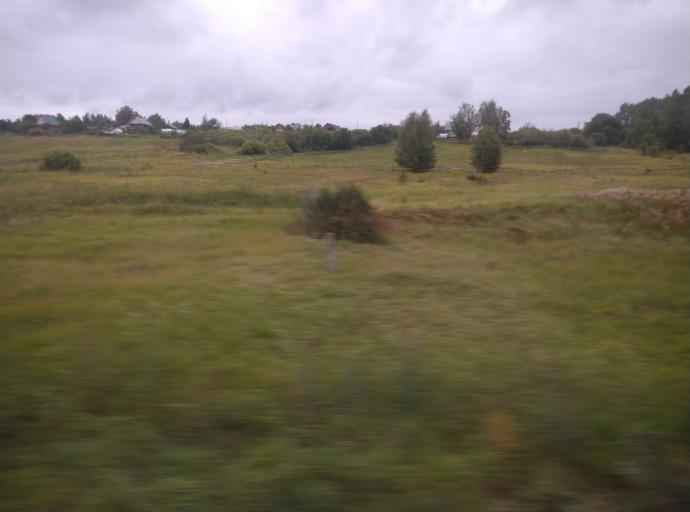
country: RU
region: Kostroma
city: Nerekhta
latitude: 57.4891
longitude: 40.6106
